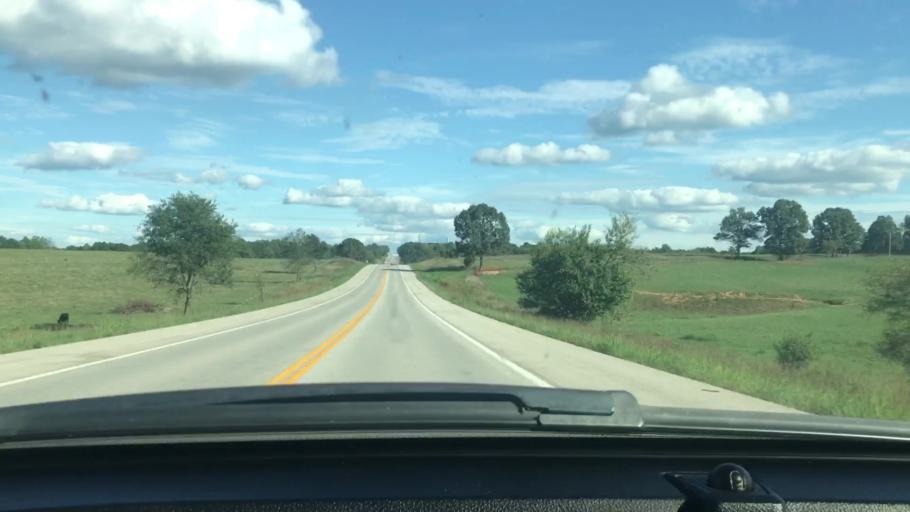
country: US
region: Missouri
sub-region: Howell County
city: West Plains
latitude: 36.6578
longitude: -91.7030
